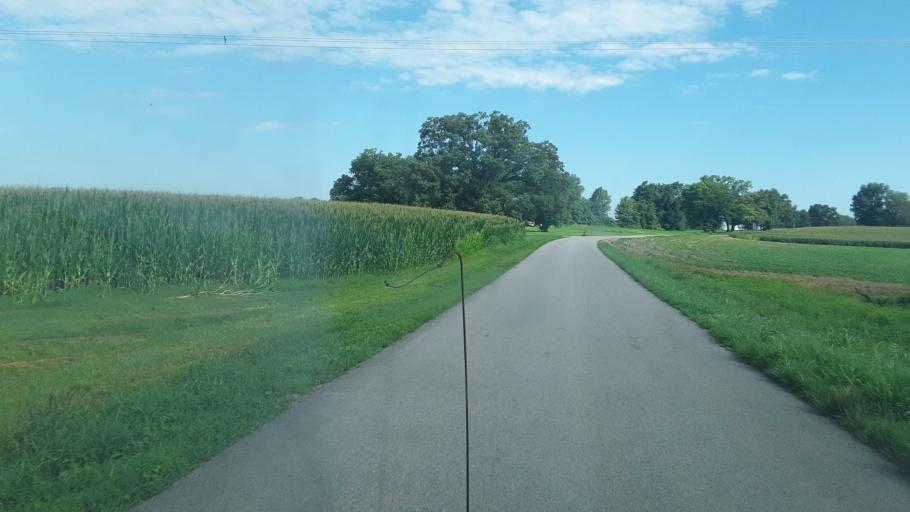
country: US
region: Kentucky
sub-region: Todd County
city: Guthrie
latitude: 36.6858
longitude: -87.1706
